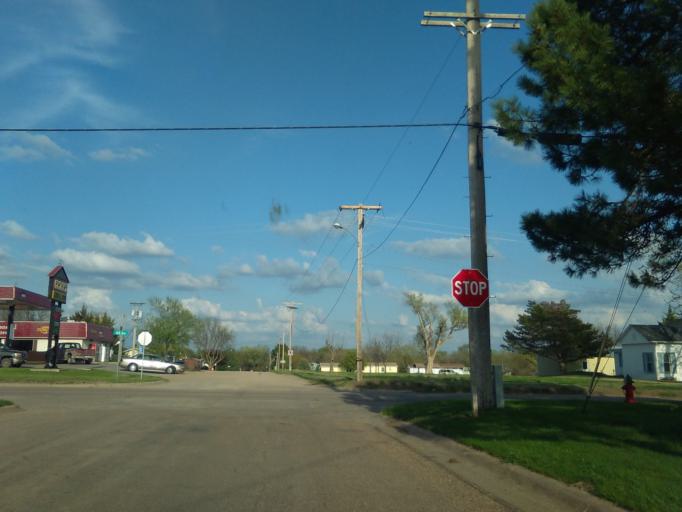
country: US
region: Nebraska
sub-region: Franklin County
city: Franklin
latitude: 40.1015
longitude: -98.9527
